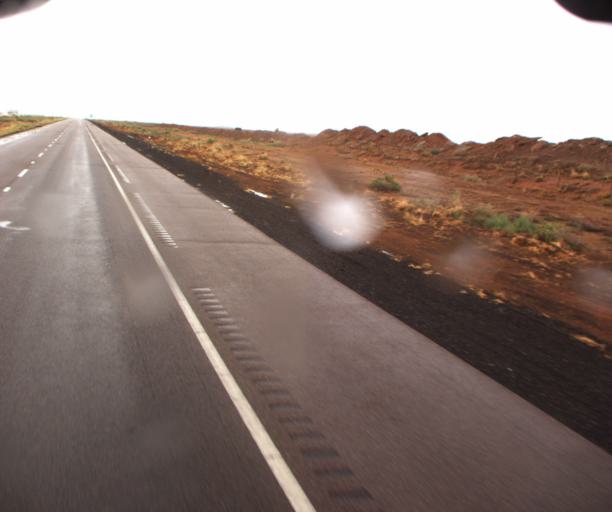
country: US
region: Arizona
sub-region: Coconino County
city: LeChee
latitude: 35.0757
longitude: -110.8642
